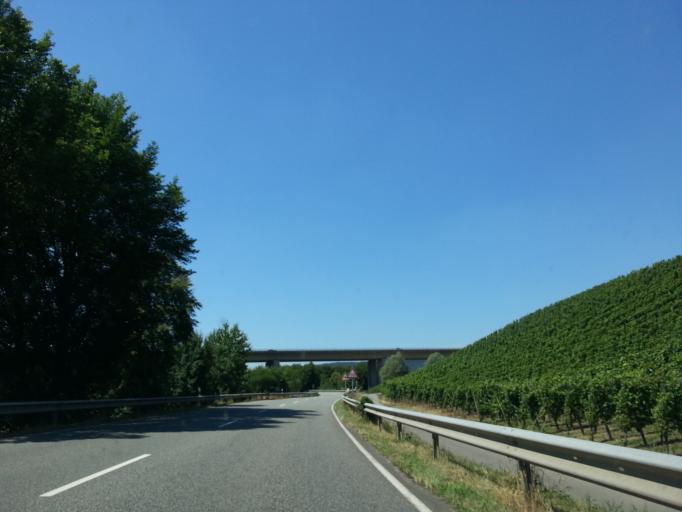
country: DE
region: Rheinland-Pfalz
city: Schweich
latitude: 49.8155
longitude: 6.7619
